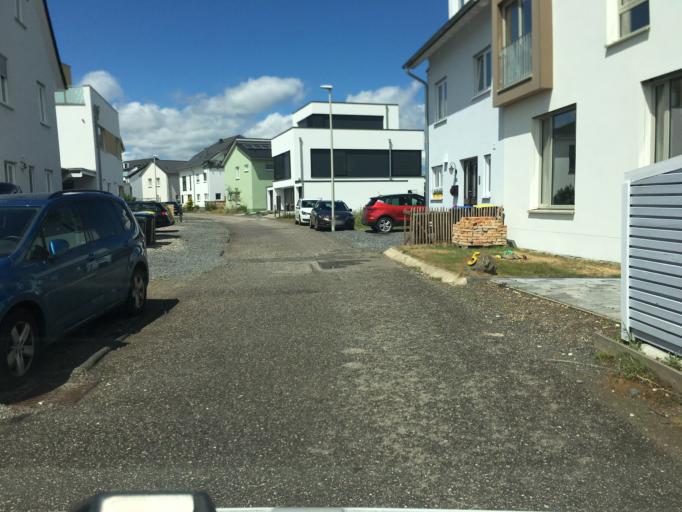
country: DE
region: North Rhine-Westphalia
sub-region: Regierungsbezirk Koln
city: Bonn
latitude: 50.7595
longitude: 7.1254
